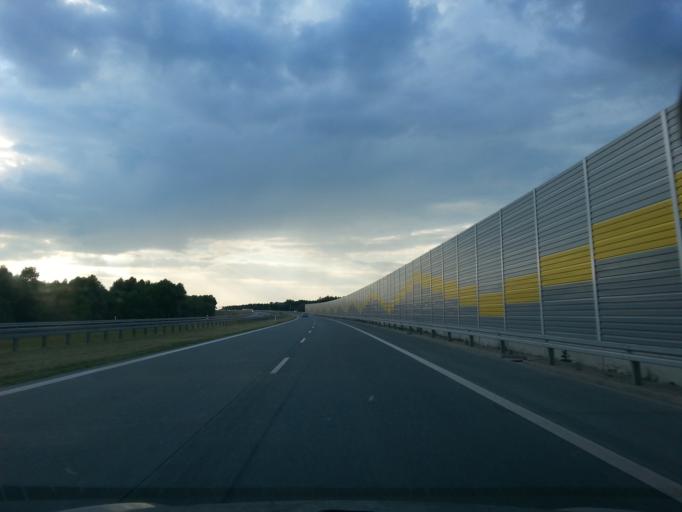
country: PL
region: Lodz Voivodeship
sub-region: Powiat zdunskowolski
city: Zapolice
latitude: 51.5903
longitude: 18.8922
